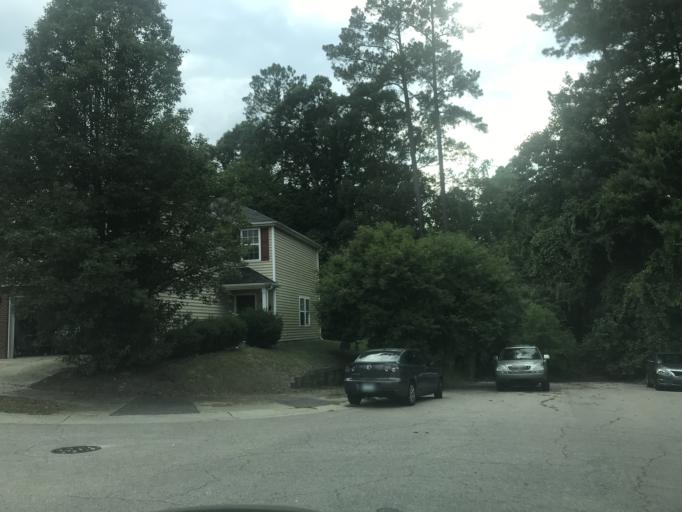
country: US
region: North Carolina
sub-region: Wake County
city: Knightdale
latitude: 35.8428
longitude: -78.5633
